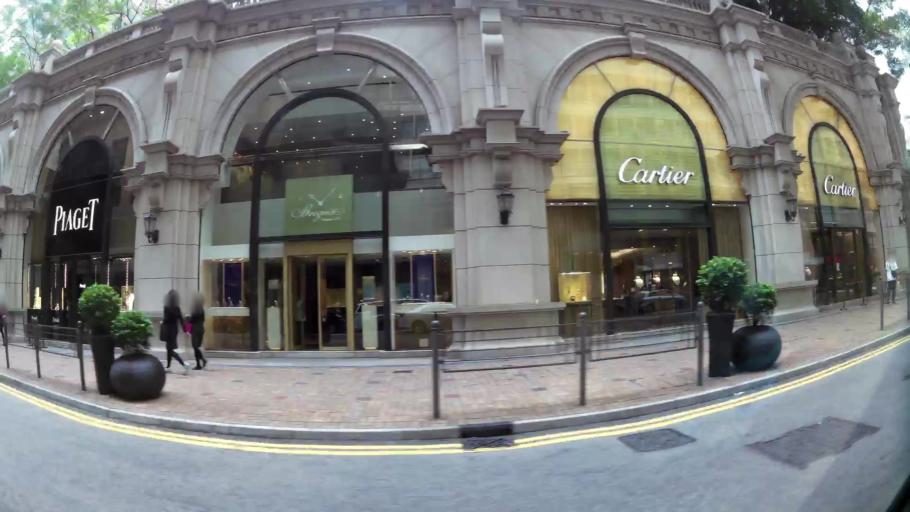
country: HK
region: Wanchai
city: Wan Chai
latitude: 22.2958
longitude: 114.1694
